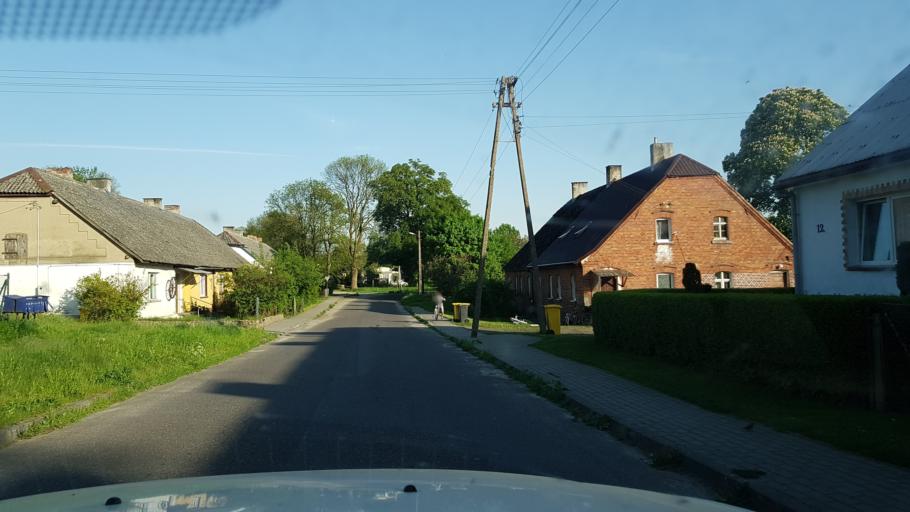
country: PL
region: West Pomeranian Voivodeship
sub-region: Powiat lobeski
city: Radowo Male
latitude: 53.6483
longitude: 15.3705
